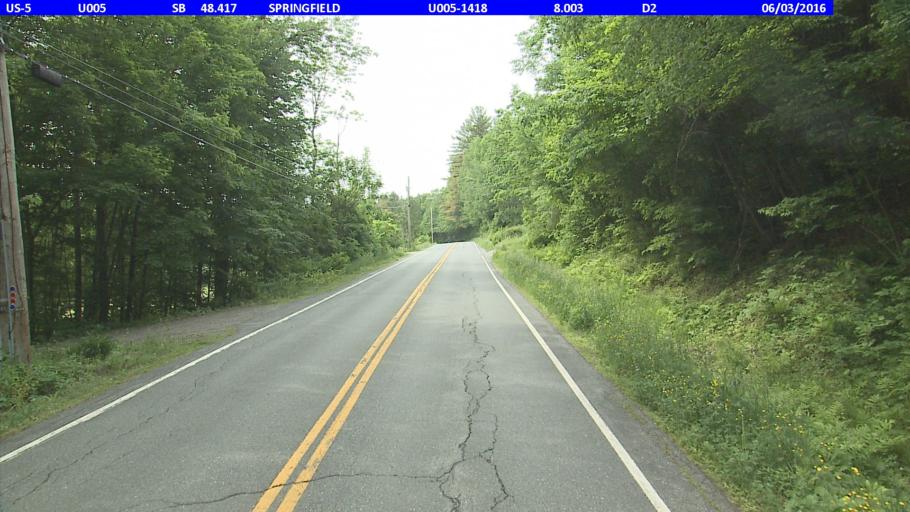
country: US
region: Vermont
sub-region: Windsor County
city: Springfield
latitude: 43.3241
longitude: -72.4074
